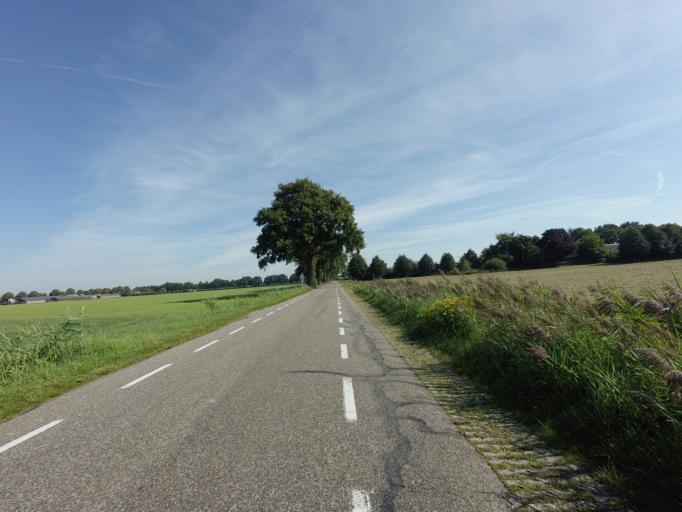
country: NL
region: Gelderland
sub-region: Oost Gelre
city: Lichtenvoorde
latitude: 52.0358
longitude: 6.5396
